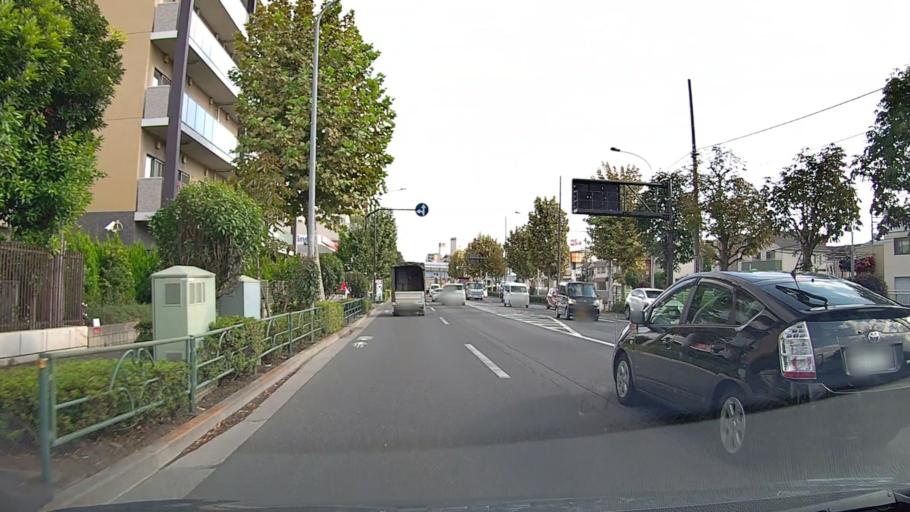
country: JP
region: Saitama
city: Wako
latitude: 35.7462
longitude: 139.6262
